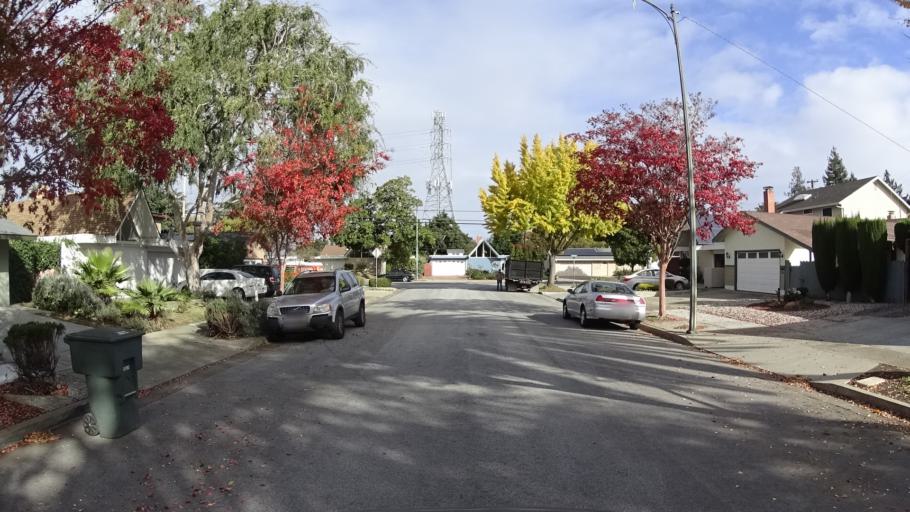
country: US
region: California
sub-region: Santa Clara County
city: Sunnyvale
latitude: 37.3623
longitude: -122.0209
